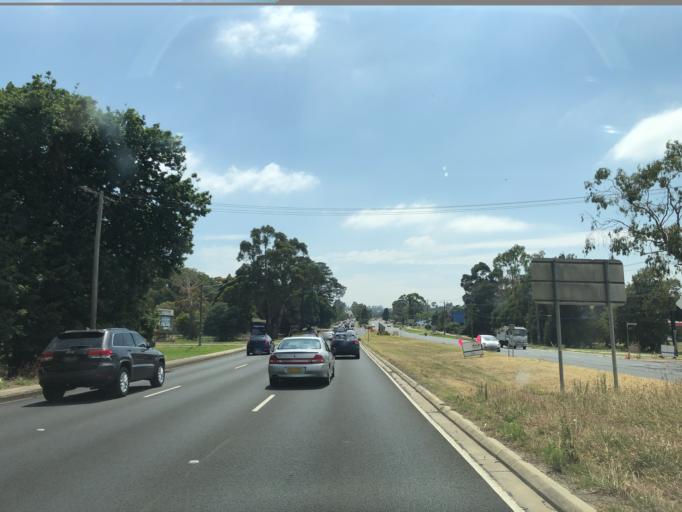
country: AU
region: Victoria
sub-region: Maroondah
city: Croydon North
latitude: -37.7692
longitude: 145.2973
